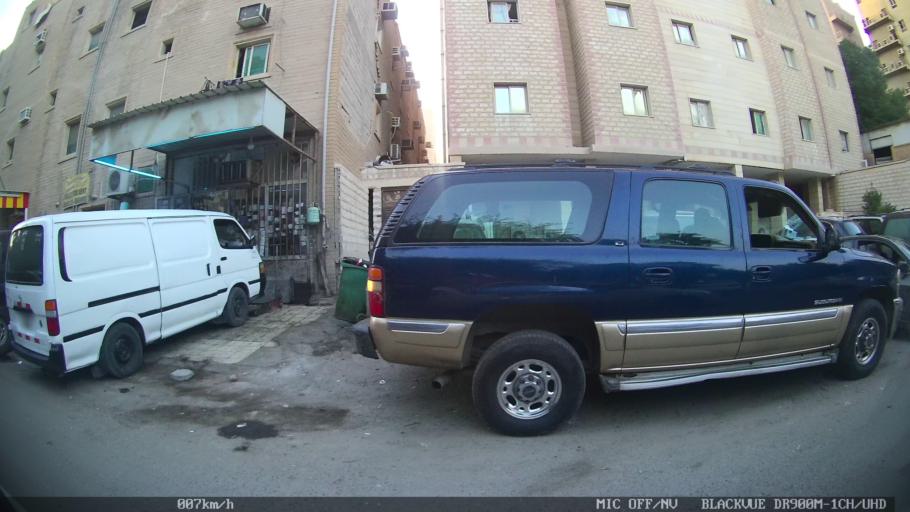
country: KW
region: Al Farwaniyah
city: Janub as Surrah
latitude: 29.2895
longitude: 47.9788
